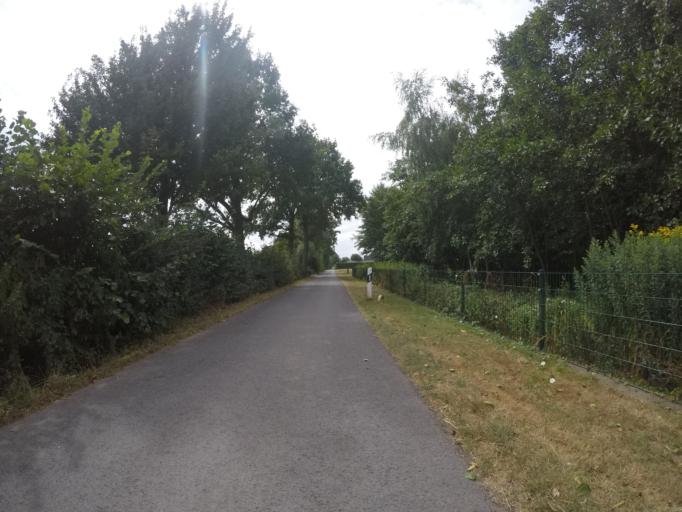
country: DE
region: North Rhine-Westphalia
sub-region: Regierungsbezirk Dusseldorf
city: Bocholt
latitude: 51.8524
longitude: 6.5591
